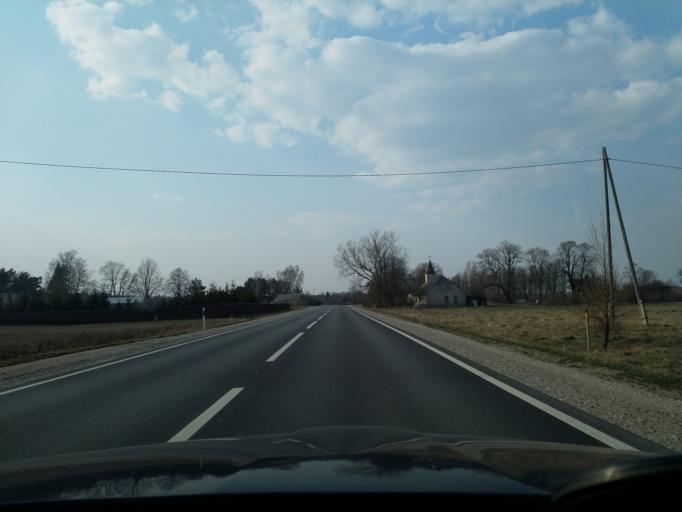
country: LV
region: Nica
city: Nica
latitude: 56.3643
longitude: 21.0047
